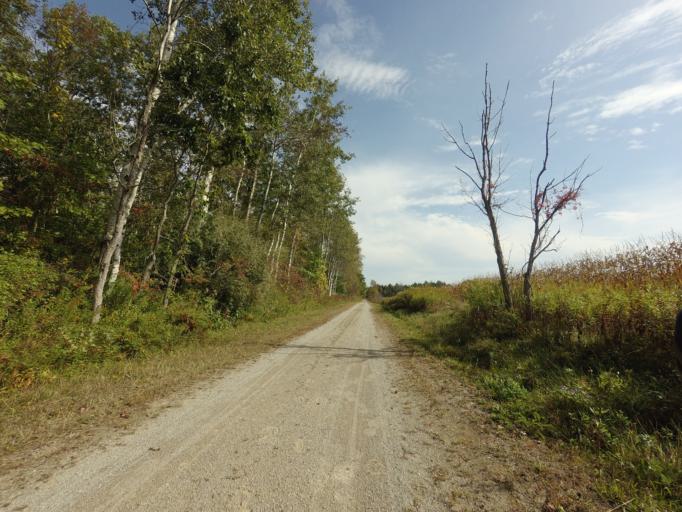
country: CA
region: Ontario
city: Brantford
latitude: 43.1826
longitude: -80.1603
